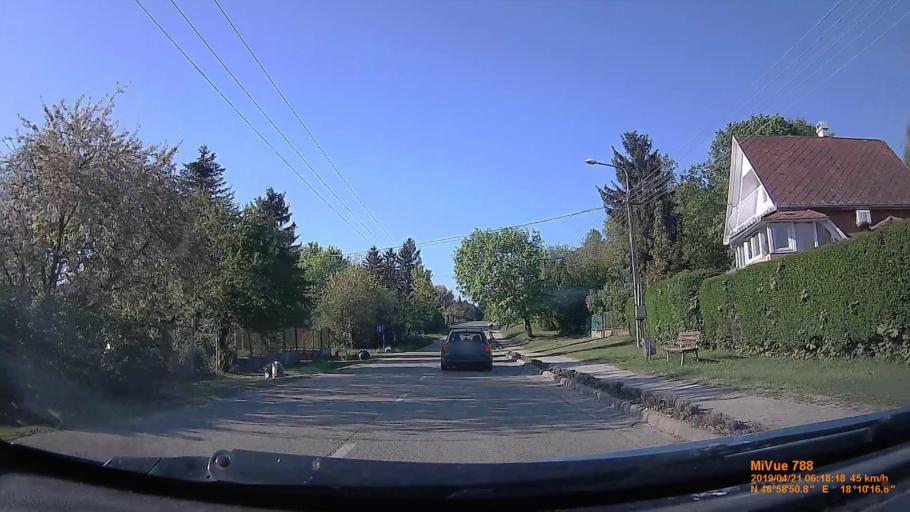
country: HU
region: Fejer
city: Lepseny
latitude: 46.9808
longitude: 18.1713
